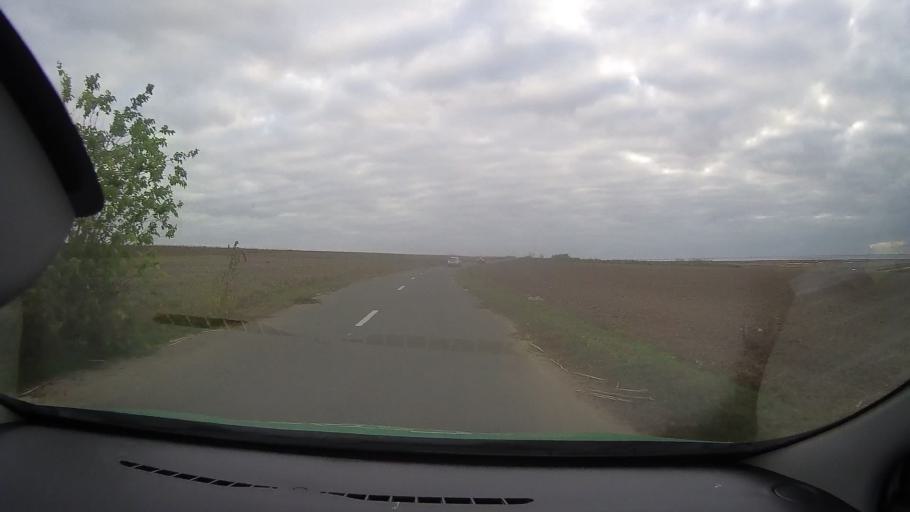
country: RO
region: Tulcea
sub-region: Comuna Jurilovca
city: Jurilovca
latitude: 44.7620
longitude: 28.8954
